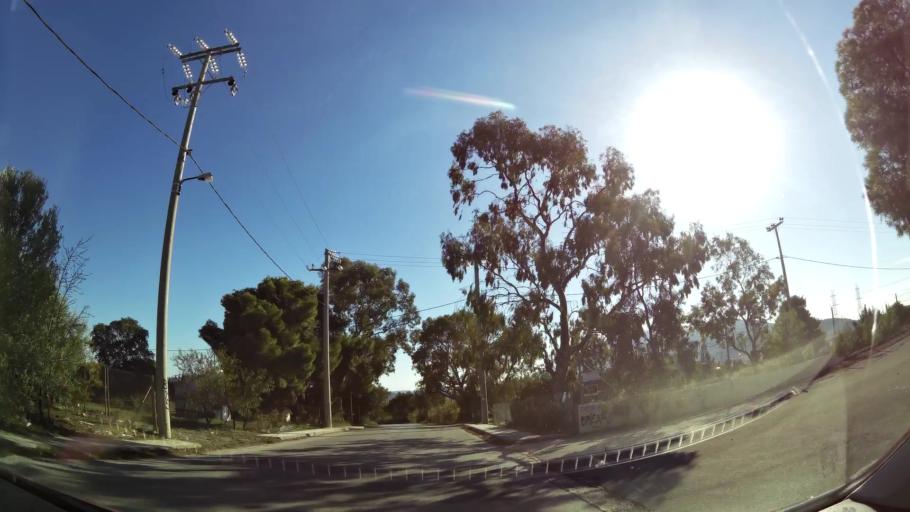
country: GR
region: Attica
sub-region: Nomarchia Anatolikis Attikis
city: Anthousa
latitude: 38.0217
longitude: 23.8675
